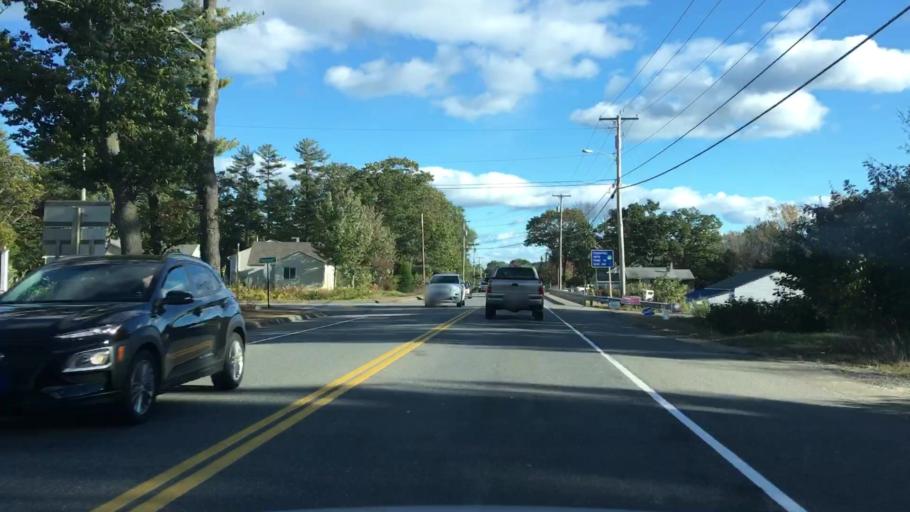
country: US
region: Maine
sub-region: York County
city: Wells Beach Station
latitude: 43.3272
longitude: -70.6186
